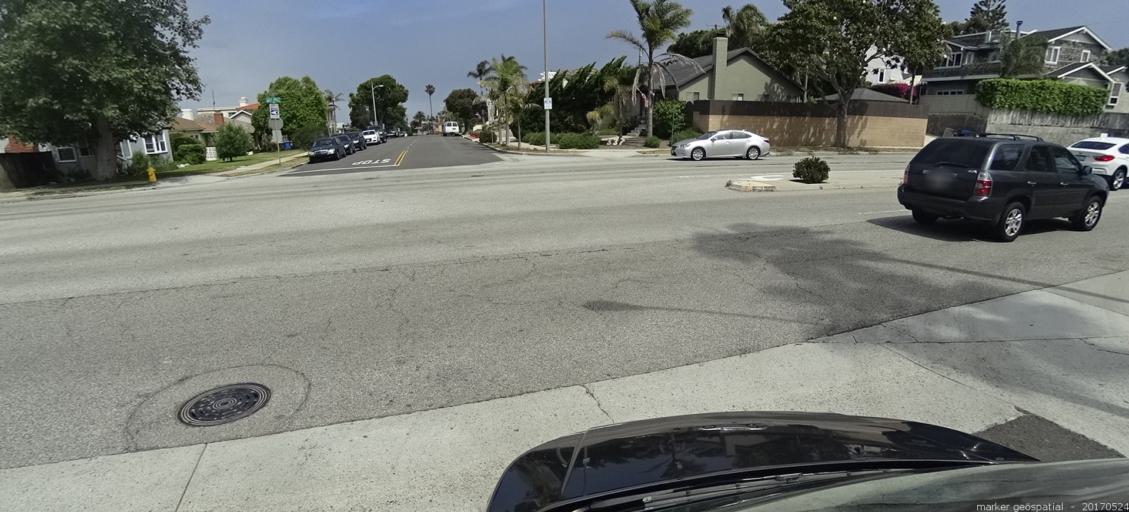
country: US
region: California
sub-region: Los Angeles County
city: Palos Verdes Estates
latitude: 33.8201
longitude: -118.3824
